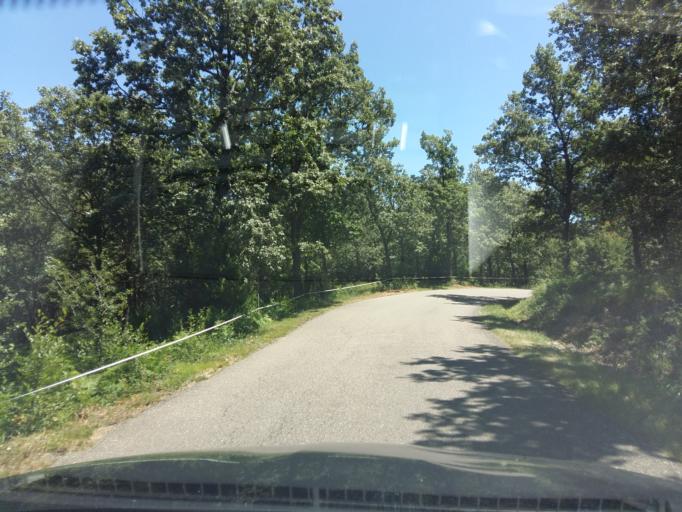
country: ES
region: Castille and Leon
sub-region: Provincia de Soria
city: Vozmediano
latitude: 41.8140
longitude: -1.8178
